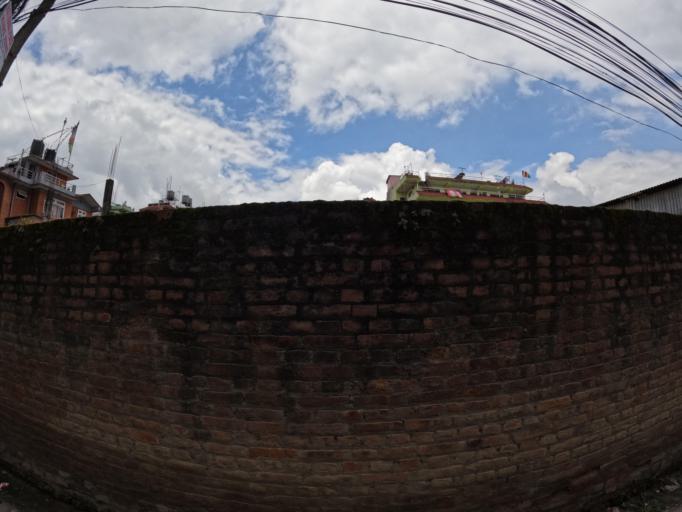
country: NP
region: Central Region
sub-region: Bagmati Zone
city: Kathmandu
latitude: 27.7381
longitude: 85.3130
